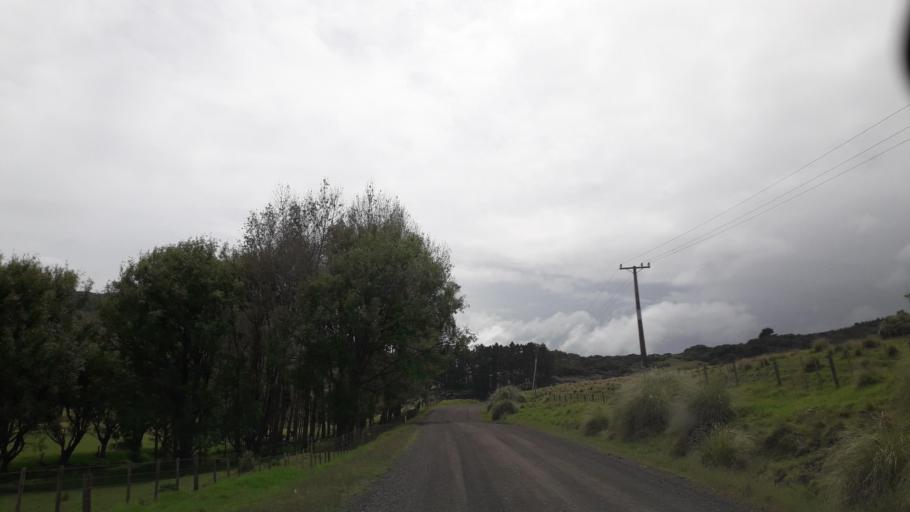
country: NZ
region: Northland
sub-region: Far North District
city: Ahipara
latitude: -35.4389
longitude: 173.3276
